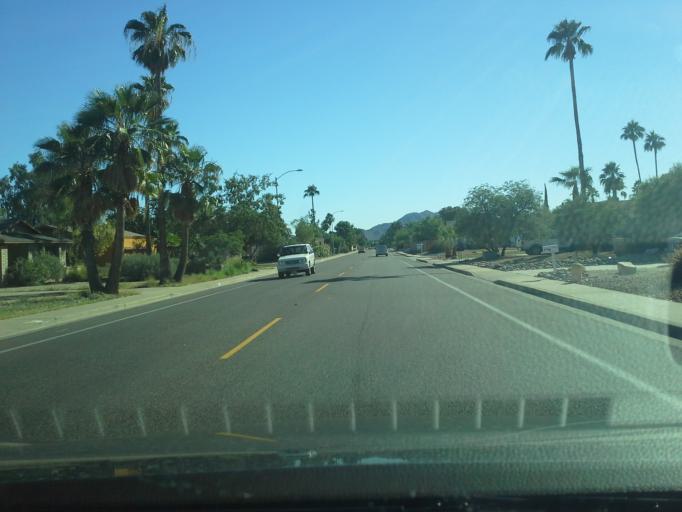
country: US
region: Arizona
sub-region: Maricopa County
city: Paradise Valley
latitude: 33.6154
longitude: -111.9866
